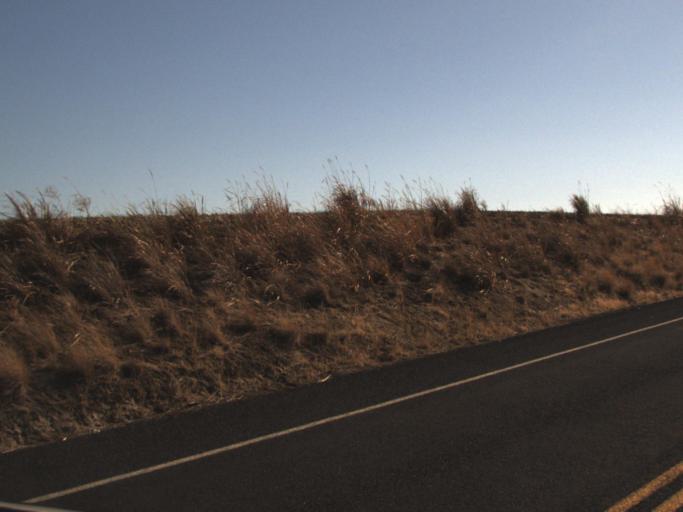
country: US
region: Washington
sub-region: Adams County
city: Ritzville
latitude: 46.9441
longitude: -118.5661
